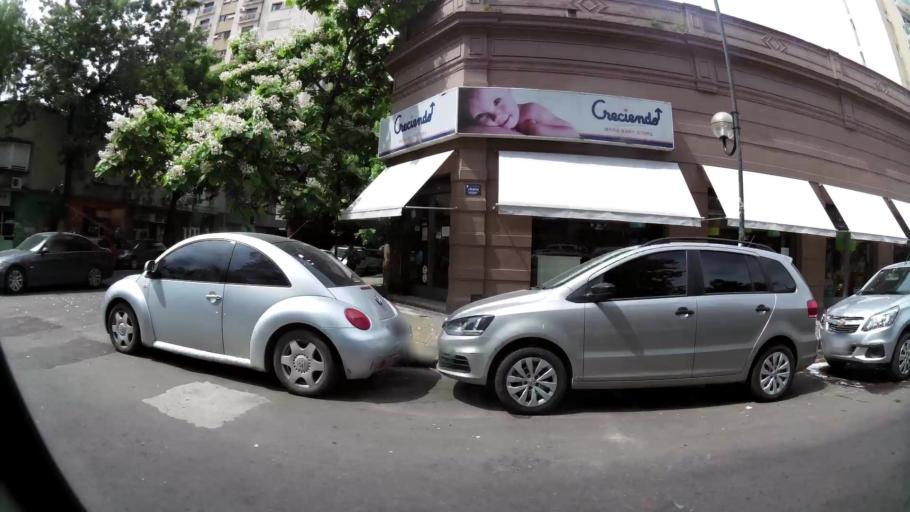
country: AR
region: Buenos Aires
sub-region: Partido de La Plata
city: La Plata
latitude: -34.9193
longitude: -57.9484
